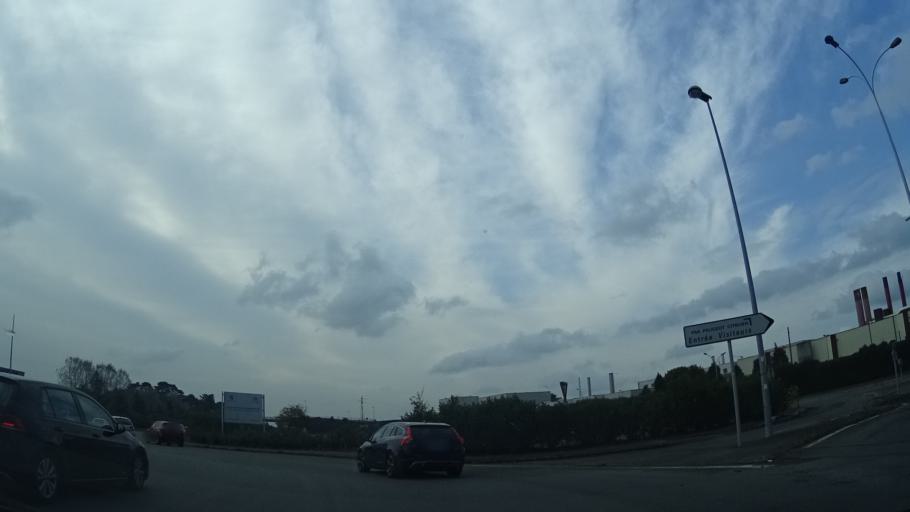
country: FR
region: Brittany
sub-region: Departement d'Ille-et-Vilaine
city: Chartres-de-Bretagne
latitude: 48.0563
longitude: -1.7036
